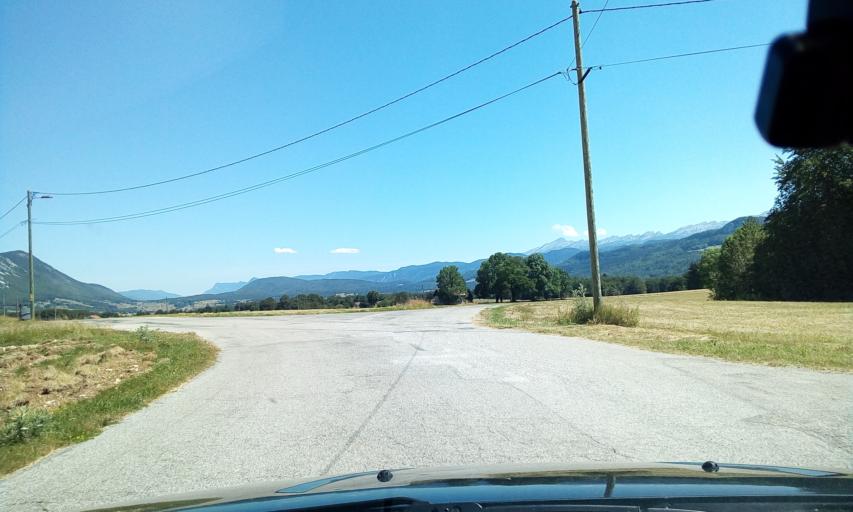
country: FR
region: Rhone-Alpes
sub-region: Departement de la Drome
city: Die
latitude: 44.8699
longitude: 5.3609
